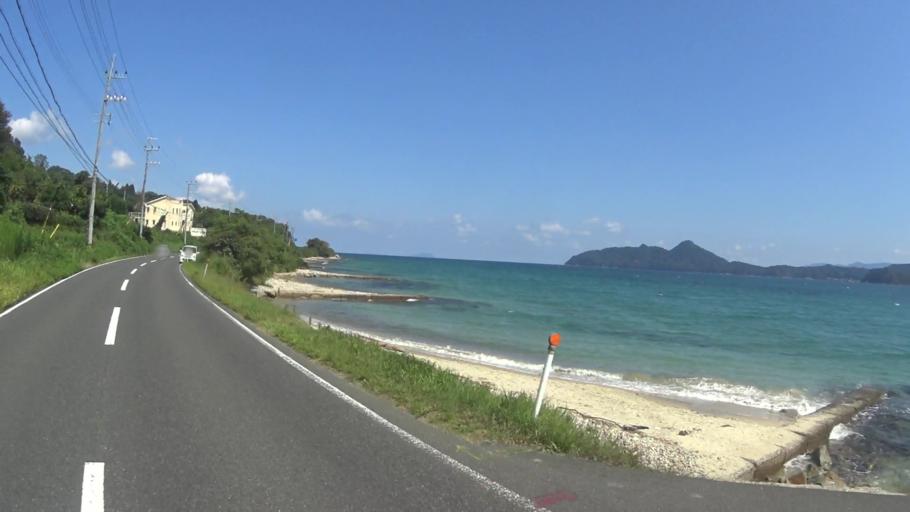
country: JP
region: Kyoto
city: Miyazu
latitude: 35.5913
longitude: 135.2090
